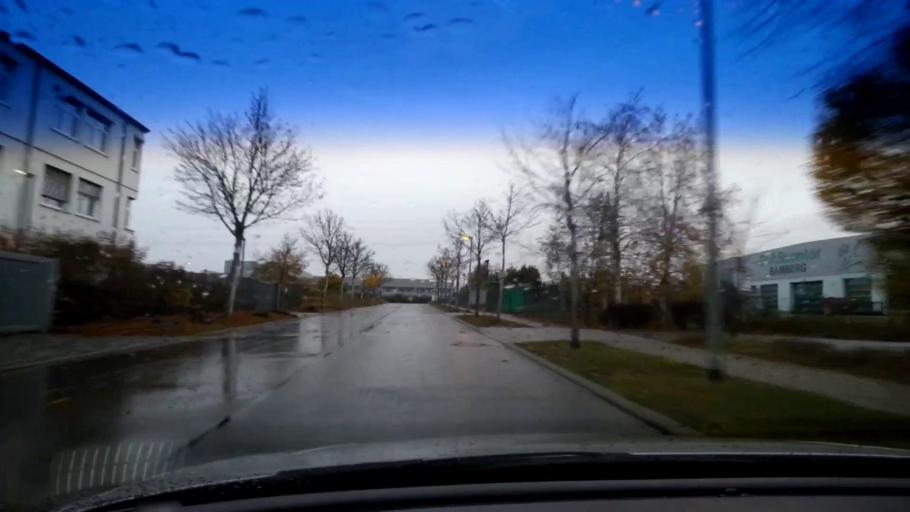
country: DE
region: Bavaria
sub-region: Upper Franconia
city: Hallstadt
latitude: 49.9185
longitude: 10.8910
